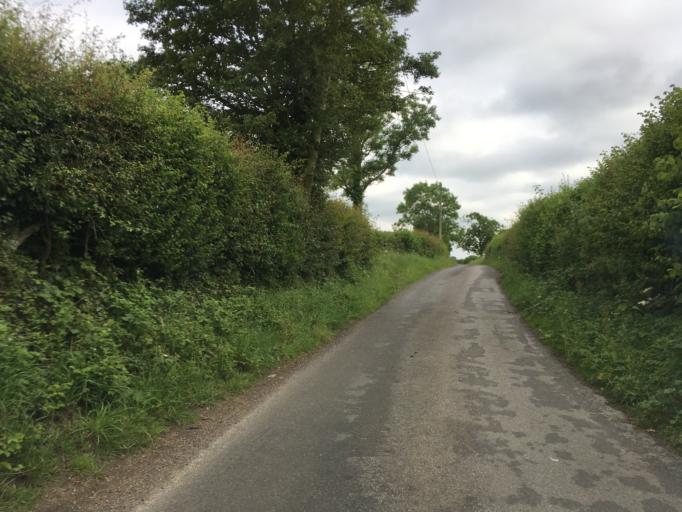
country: GB
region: England
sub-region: South Gloucestershire
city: Horton
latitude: 51.5745
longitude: -2.3495
